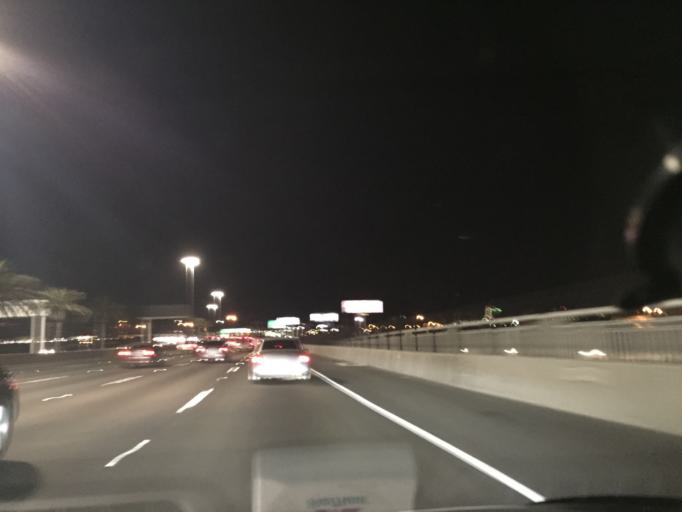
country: US
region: California
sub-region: Alameda County
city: Emeryville
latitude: 37.8218
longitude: -122.3278
